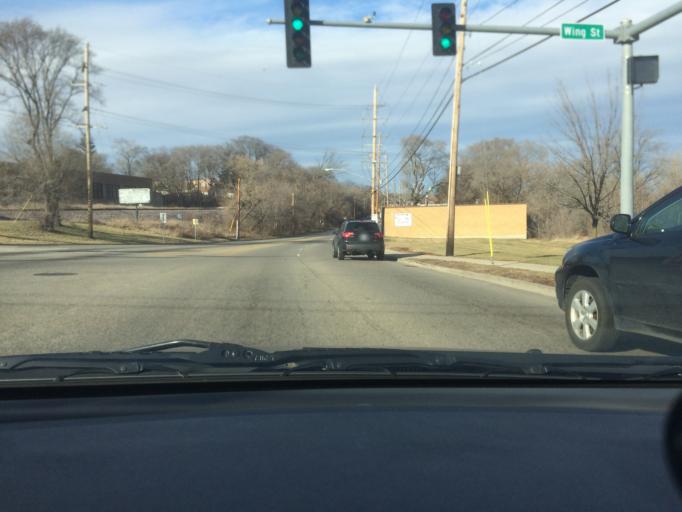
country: US
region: Illinois
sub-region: Kane County
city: Elgin
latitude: 42.0450
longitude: -88.2932
